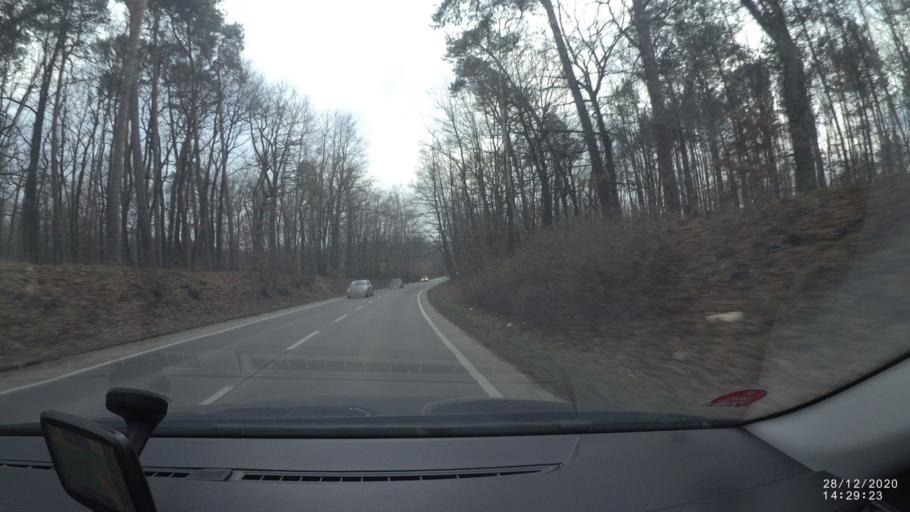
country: CZ
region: Central Bohemia
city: Sestajovice
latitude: 50.0852
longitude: 14.6657
